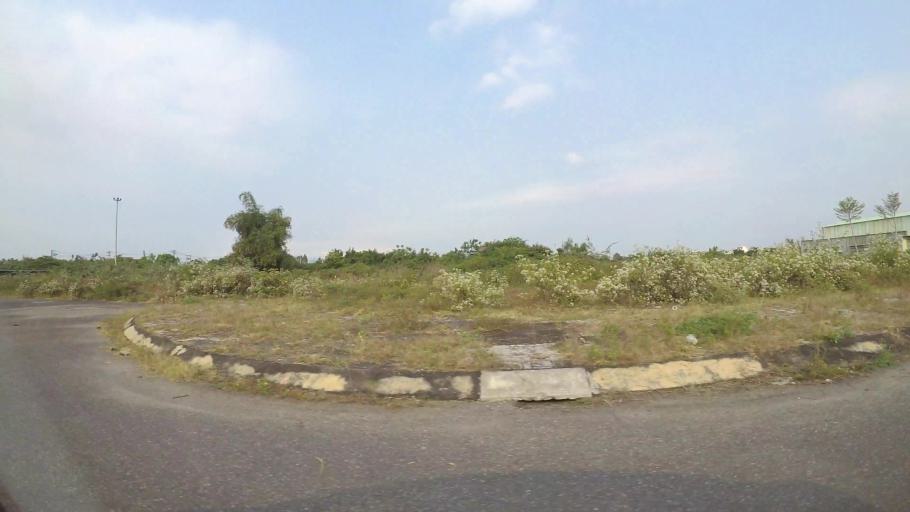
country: VN
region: Da Nang
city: Lien Chieu
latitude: 16.0479
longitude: 108.1603
